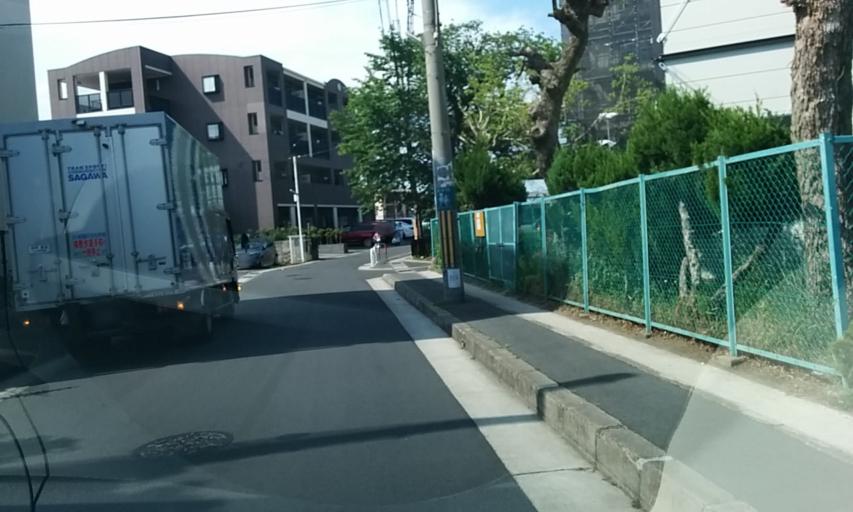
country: JP
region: Kyoto
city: Muko
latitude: 34.9265
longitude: 135.7013
